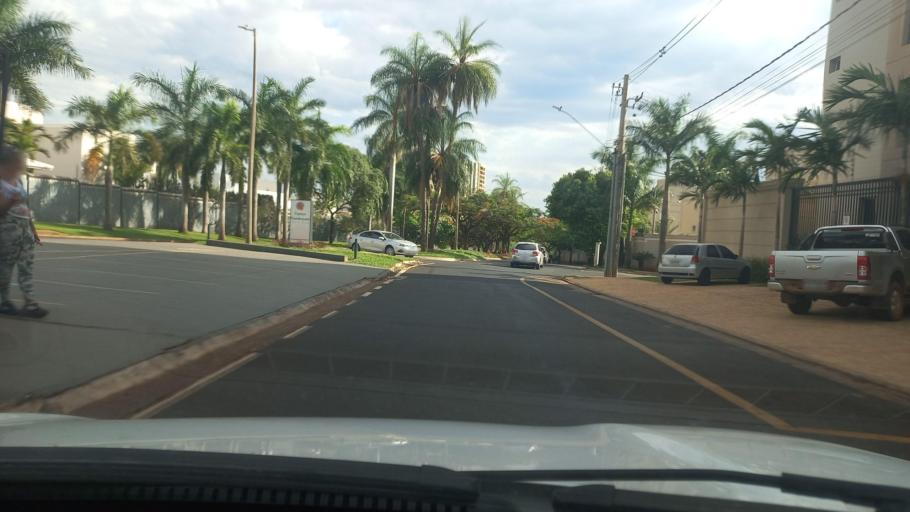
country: BR
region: Minas Gerais
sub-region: Uberaba
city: Uberaba
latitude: -19.7475
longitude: -47.9107
